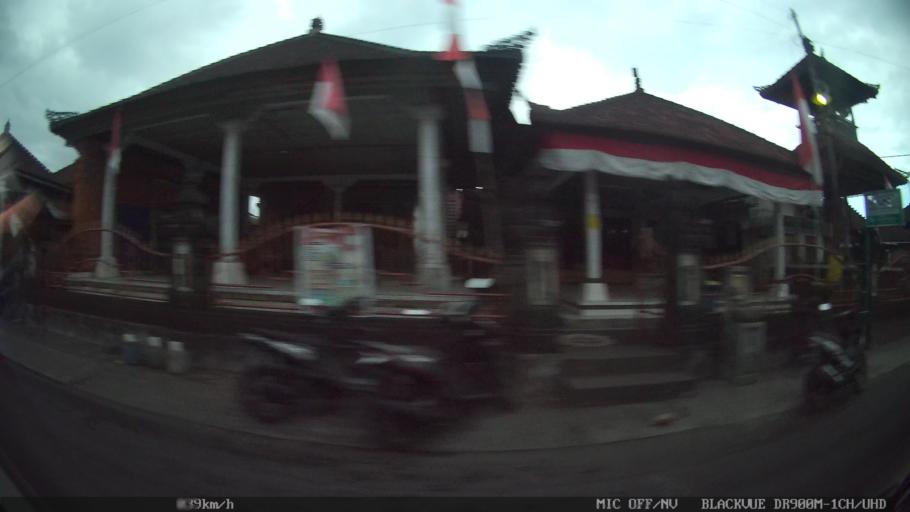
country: ID
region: Bali
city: Banjar Pasekan
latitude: -8.6194
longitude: 115.2980
